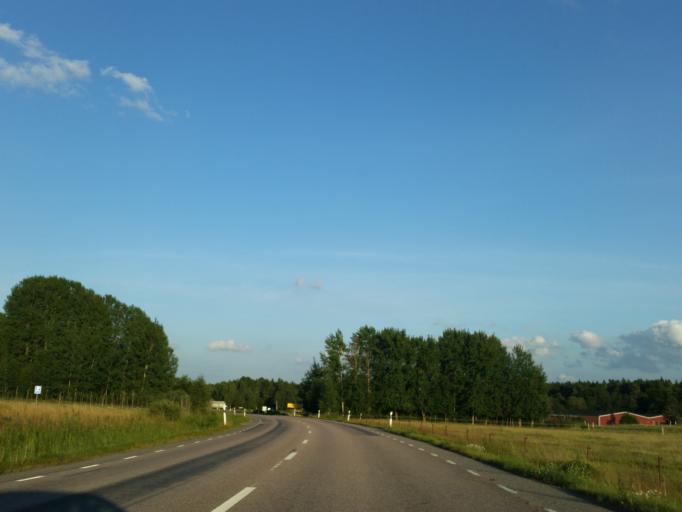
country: SE
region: Stockholm
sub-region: Sodertalje Kommun
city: Soedertaelje
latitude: 59.2220
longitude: 17.5669
